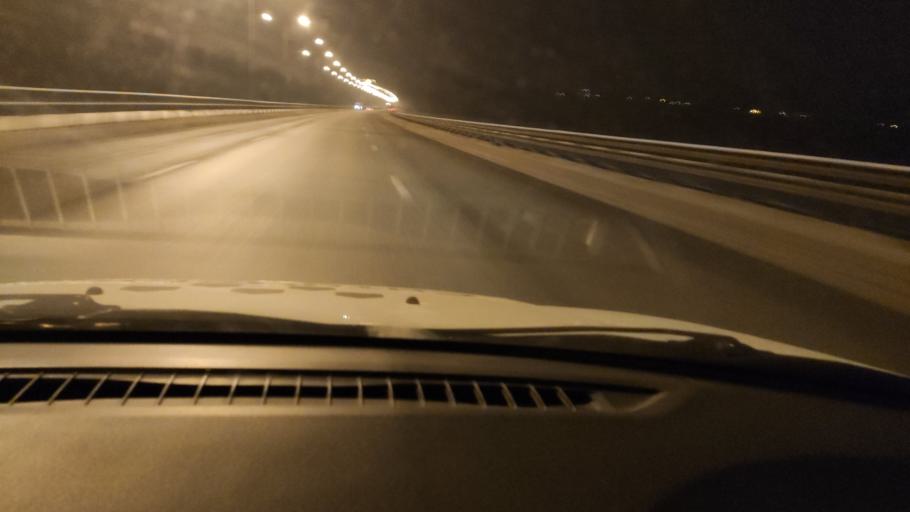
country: RU
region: Perm
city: Bershet'
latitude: 57.7102
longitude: 56.3648
